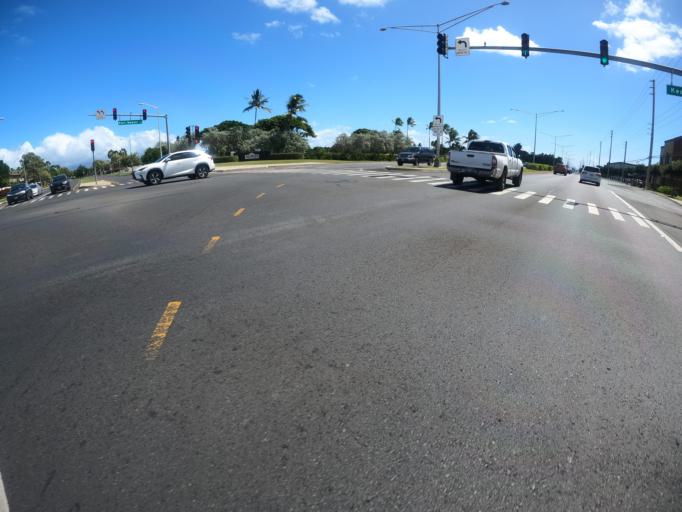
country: US
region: Hawaii
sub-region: Honolulu County
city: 'Ewa Gentry
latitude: 21.3288
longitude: -158.0205
